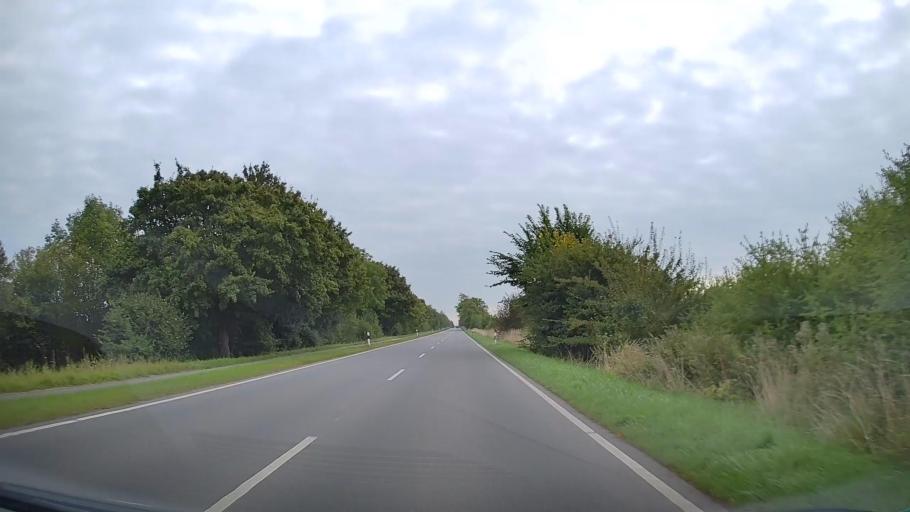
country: DE
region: Schleswig-Holstein
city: Stakendorf
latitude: 54.3920
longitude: 10.4268
